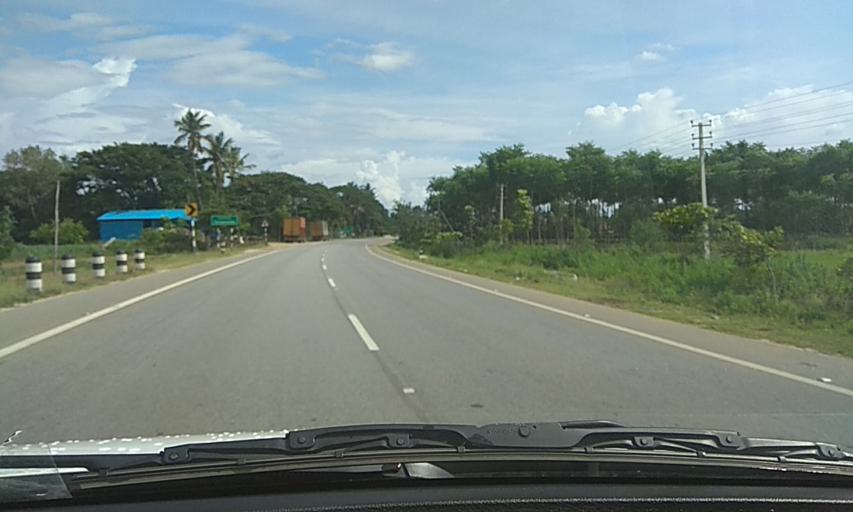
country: IN
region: Karnataka
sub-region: Mandya
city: Maddur
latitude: 12.6491
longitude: 77.0543
